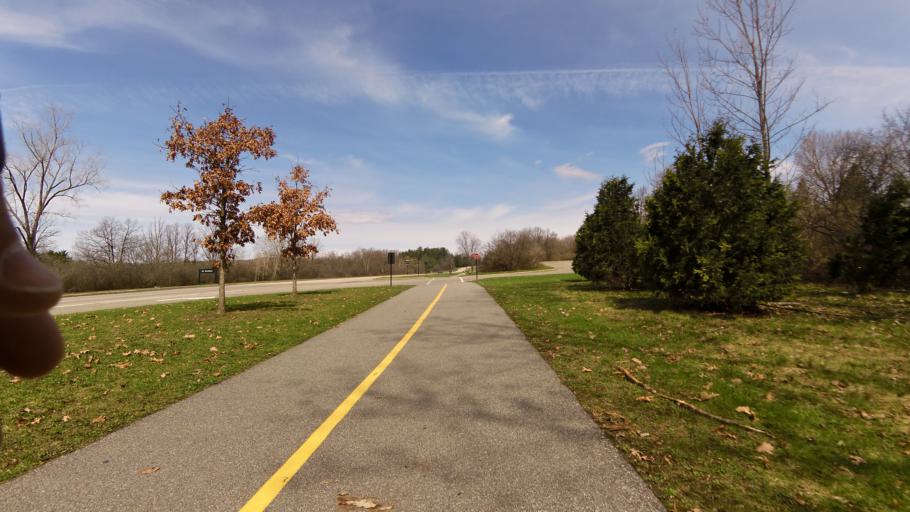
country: CA
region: Ontario
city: Ottawa
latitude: 45.4350
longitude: -75.7465
